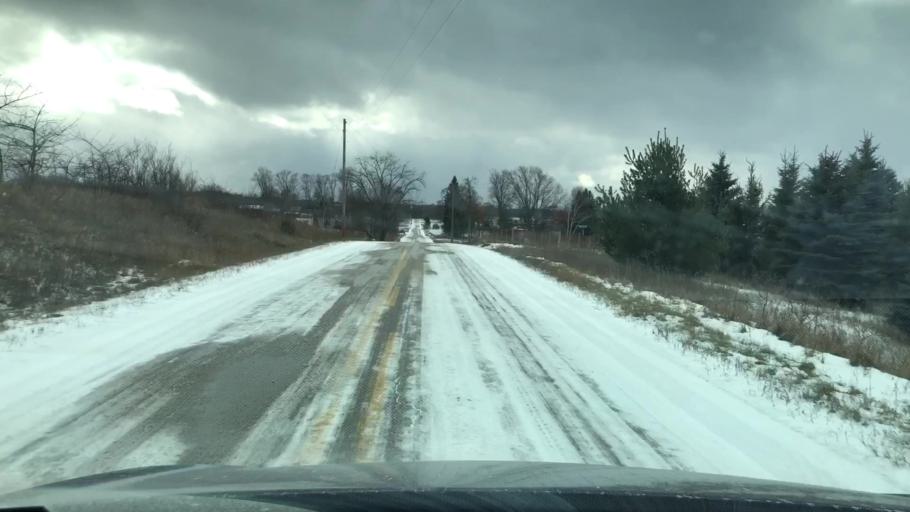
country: US
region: Michigan
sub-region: Antrim County
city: Elk Rapids
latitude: 44.9288
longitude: -85.5156
